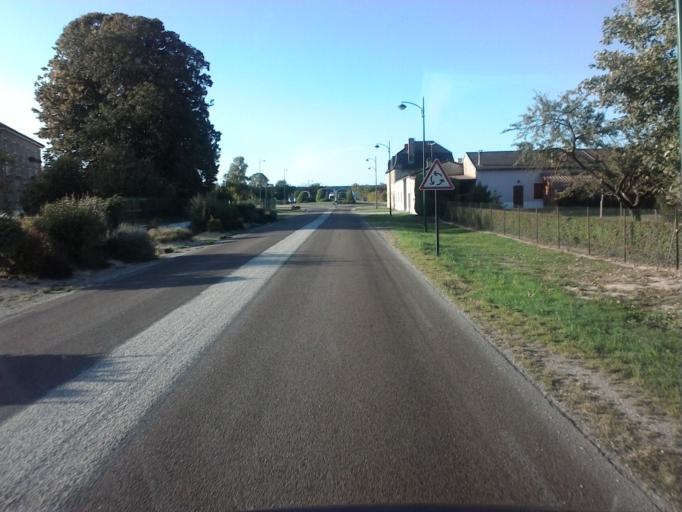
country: FR
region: Champagne-Ardenne
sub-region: Departement de l'Aube
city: Mailly-le-Camp
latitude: 48.7353
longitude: 4.2053
